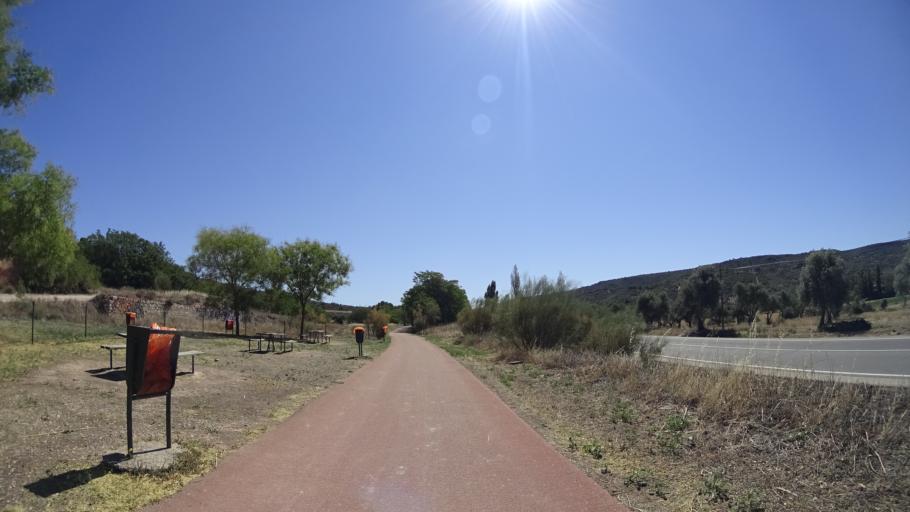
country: ES
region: Madrid
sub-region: Provincia de Madrid
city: Perales de Tajuna
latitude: 40.2316
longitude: -3.3892
